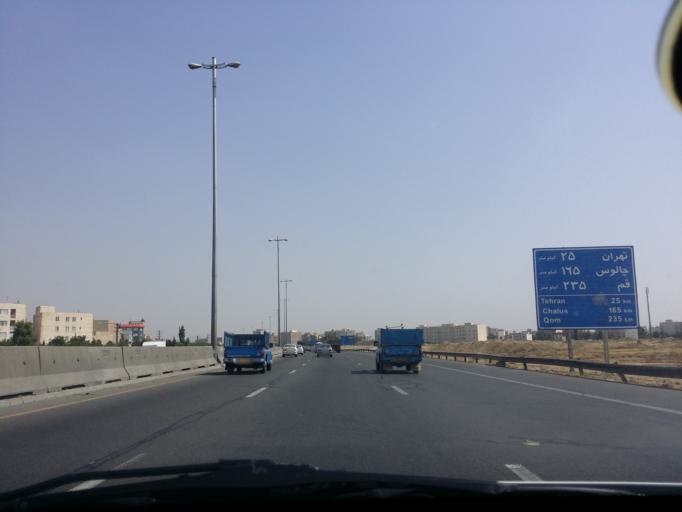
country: IR
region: Alborz
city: Karaj
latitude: 35.8320
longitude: 50.9105
